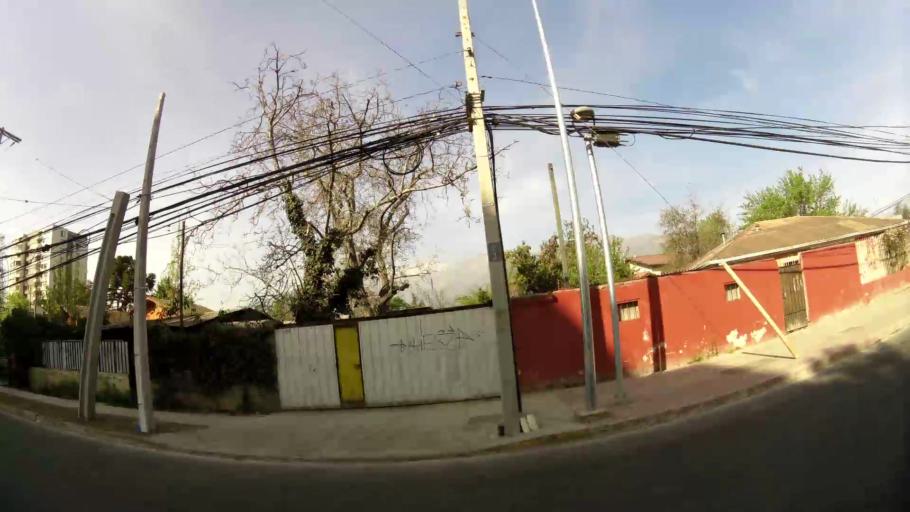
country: CL
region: Santiago Metropolitan
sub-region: Provincia de Santiago
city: Villa Presidente Frei, Nunoa, Santiago, Chile
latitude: -33.5262
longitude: -70.5890
